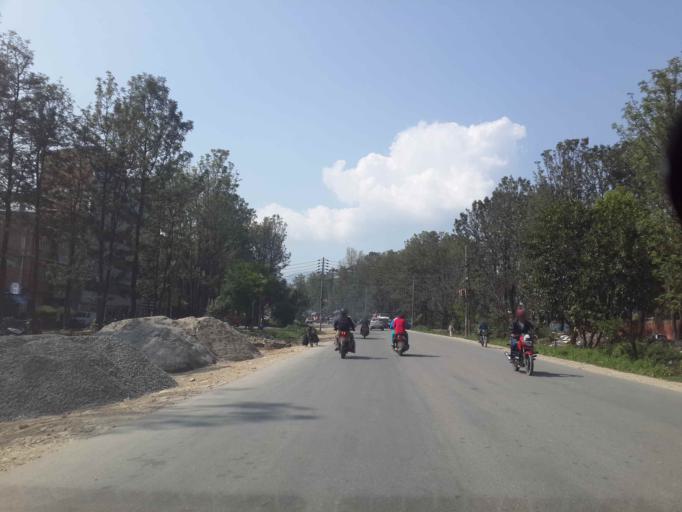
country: NP
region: Central Region
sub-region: Bagmati Zone
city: Kathmandu
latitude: 27.7372
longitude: 85.3410
